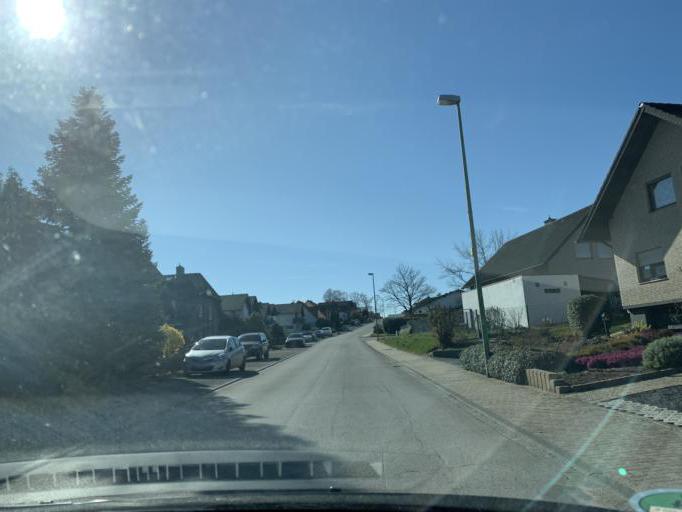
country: DE
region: North Rhine-Westphalia
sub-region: Regierungsbezirk Koln
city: Nideggen
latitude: 50.6945
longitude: 6.4877
